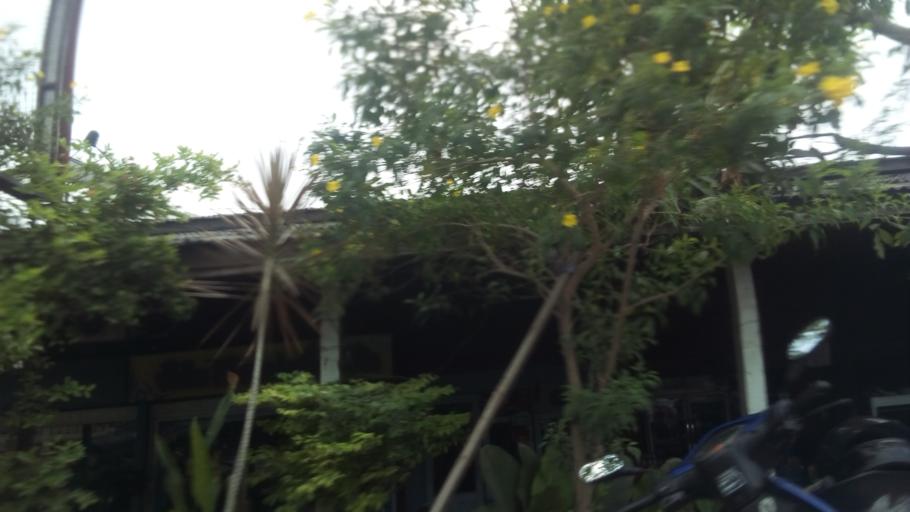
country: TH
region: Nakhon Pathom
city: Sam Phran
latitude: 13.7461
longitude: 100.2759
